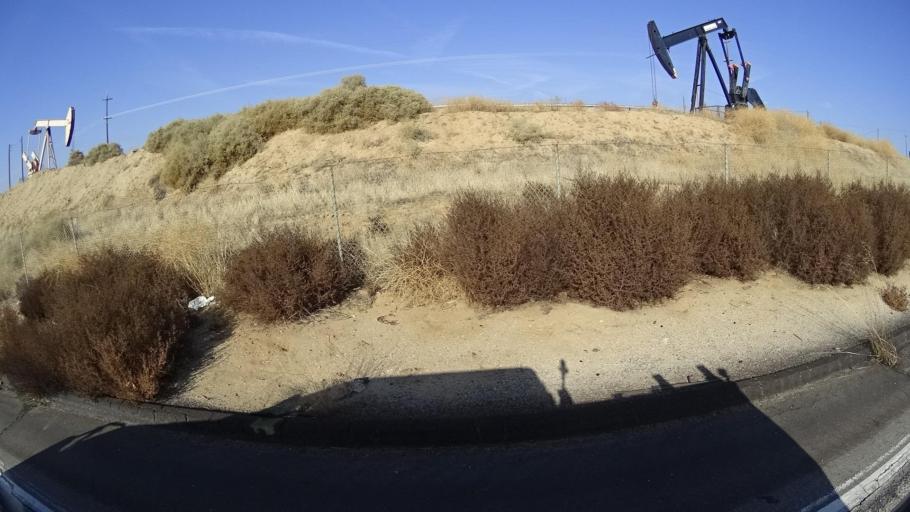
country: US
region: California
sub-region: Kern County
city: Oildale
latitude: 35.4812
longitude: -119.0138
